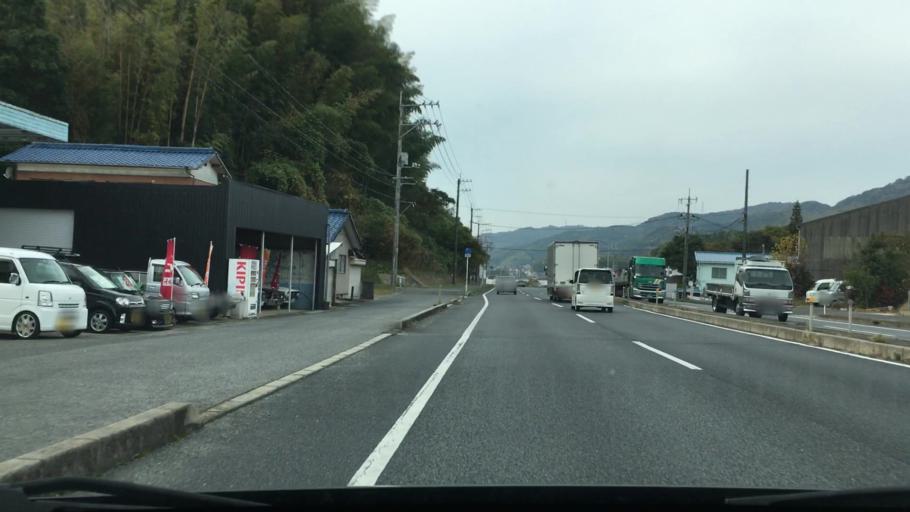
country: JP
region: Yamaguchi
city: Kudamatsu
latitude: 34.0333
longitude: 131.8961
